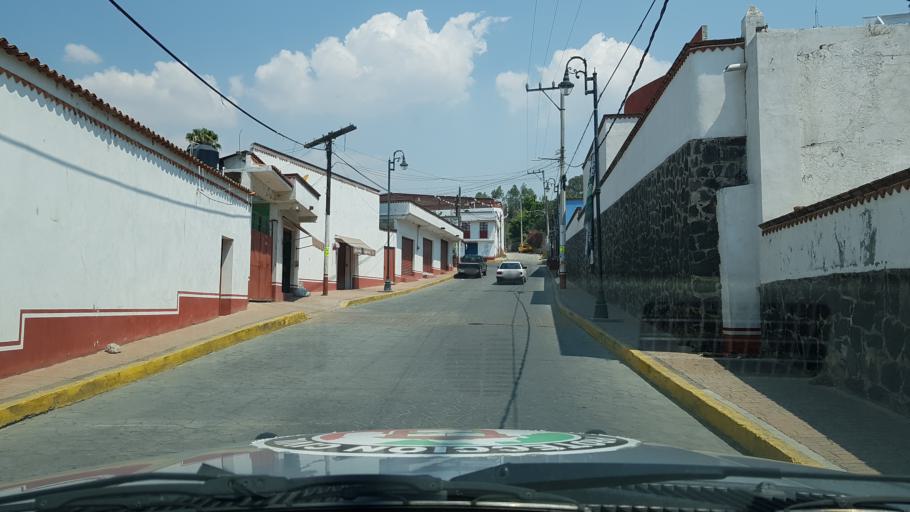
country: MX
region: Mexico
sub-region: Tepetlixpa
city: Nepantla de Sor Juana Ines de la Cruz
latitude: 18.9804
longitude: -98.8407
